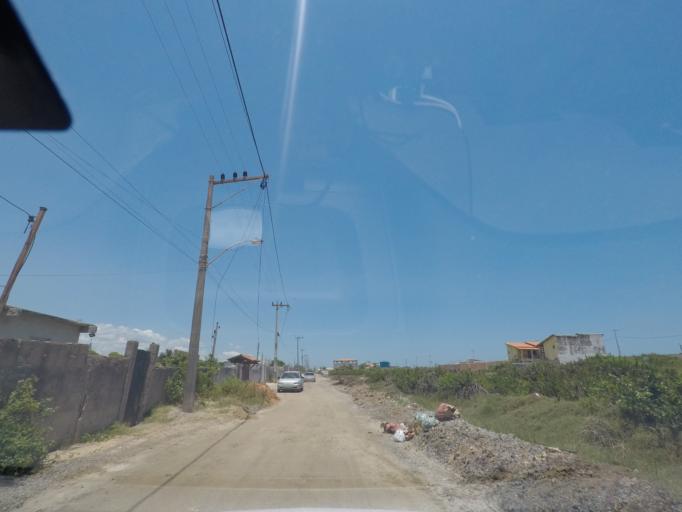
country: BR
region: Rio de Janeiro
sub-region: Niteroi
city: Niteroi
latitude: -22.9681
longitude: -42.9775
